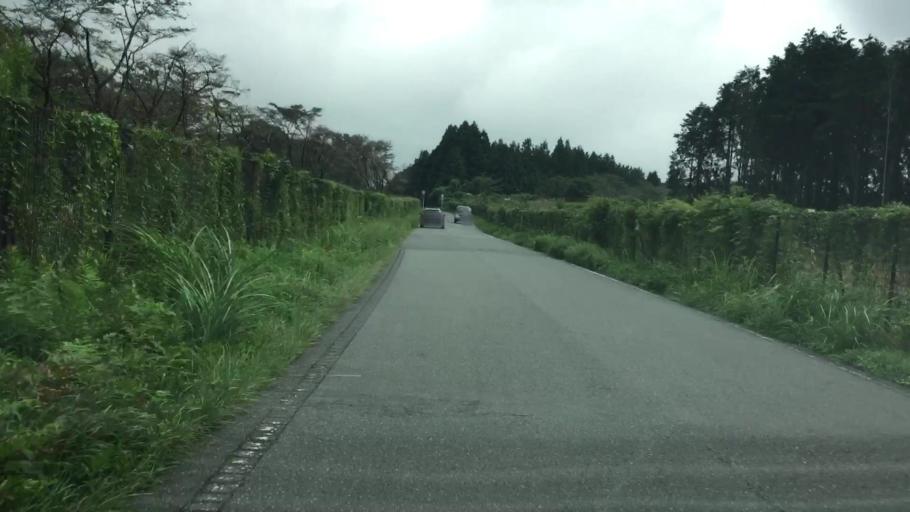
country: JP
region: Shizuoka
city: Fujinomiya
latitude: 35.3709
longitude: 138.5799
